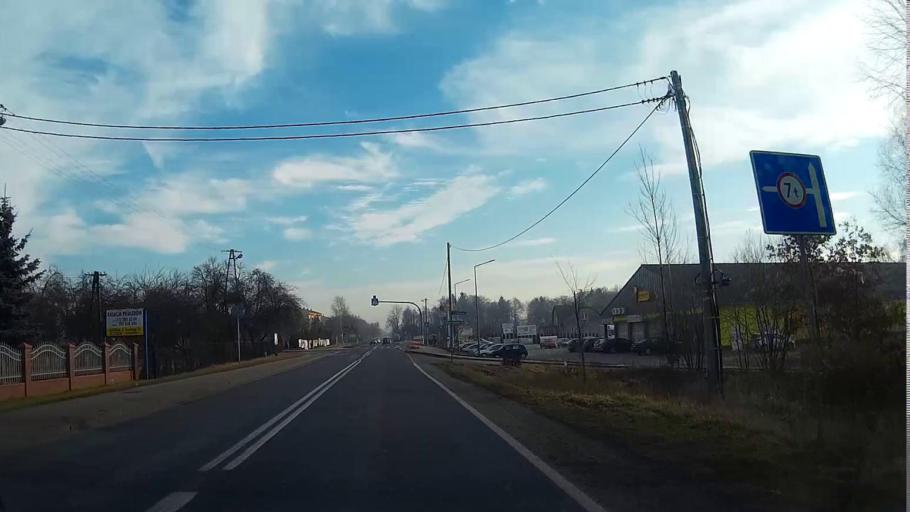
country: PL
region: Lesser Poland Voivodeship
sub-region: Powiat chrzanowski
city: Alwernia
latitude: 50.0597
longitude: 19.5389
